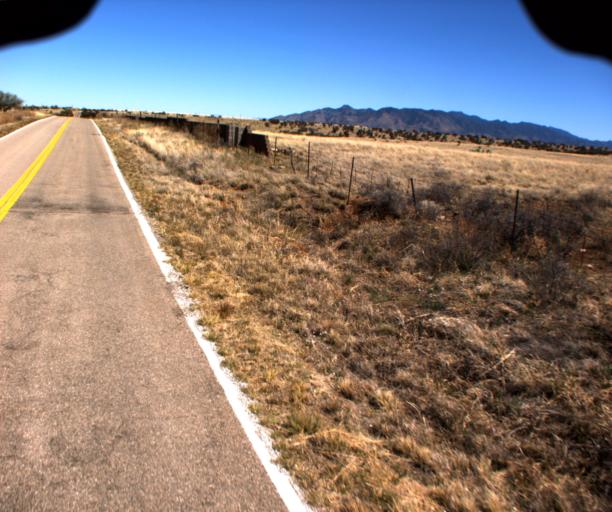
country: US
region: Arizona
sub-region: Cochise County
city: Huachuca City
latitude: 31.6007
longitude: -110.5689
